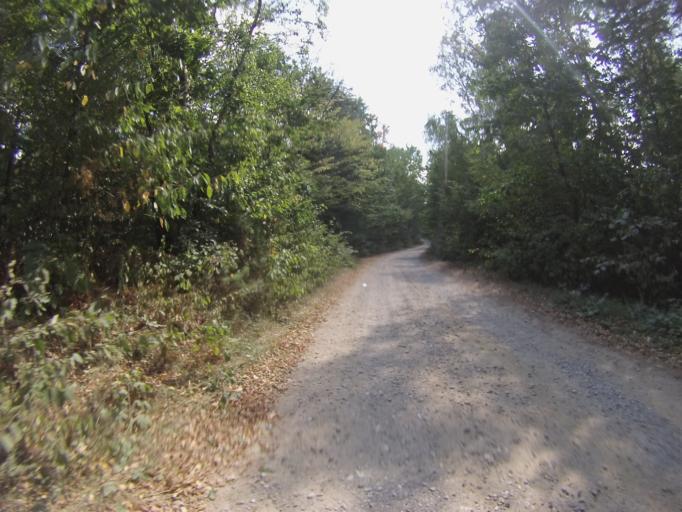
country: PL
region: Swietokrzyskie
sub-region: Powiat kielecki
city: Rakow
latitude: 50.7133
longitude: 21.0569
